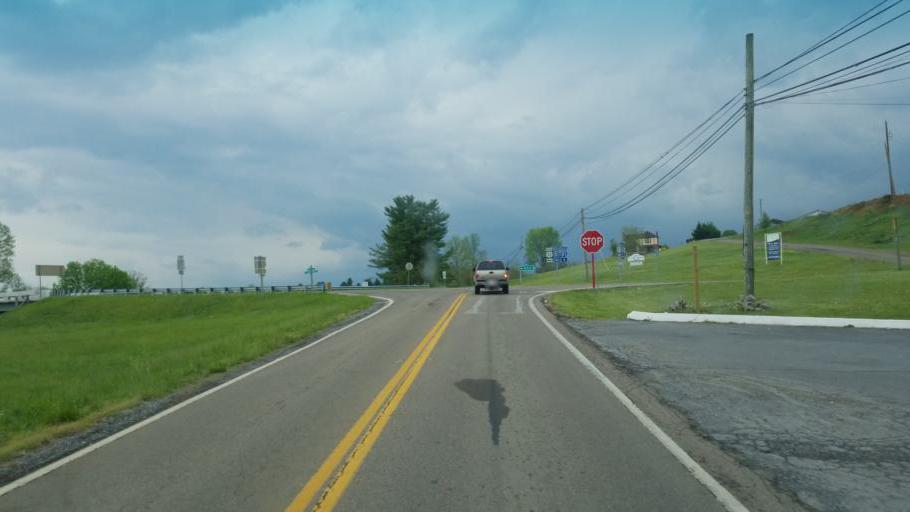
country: US
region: Virginia
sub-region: Washington County
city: Glade Spring
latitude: 36.7840
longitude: -81.7349
